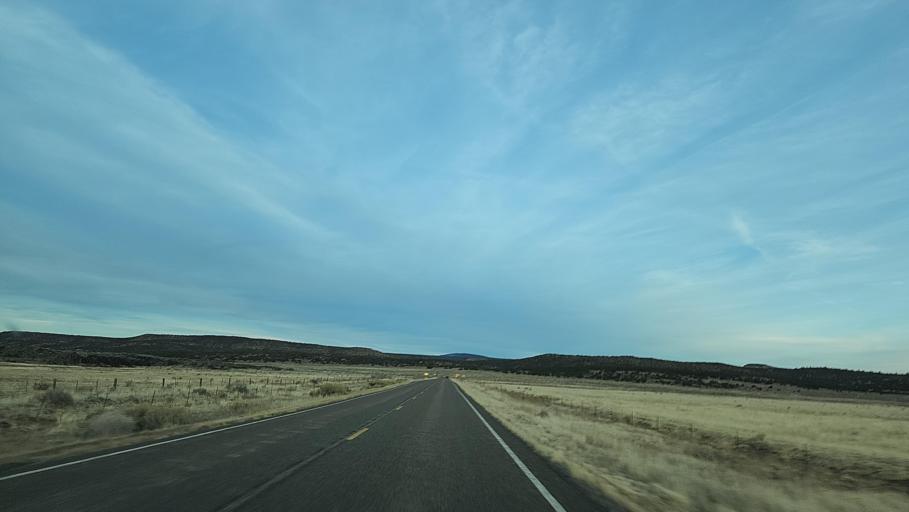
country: US
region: New Mexico
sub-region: Cibola County
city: Grants
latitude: 34.7098
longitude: -107.9967
